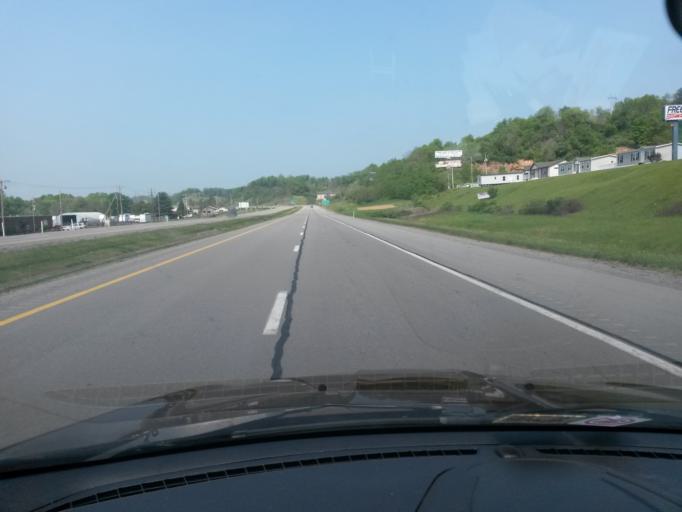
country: US
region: West Virginia
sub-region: Upshur County
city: Buckhannon
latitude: 39.0014
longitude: -80.2184
